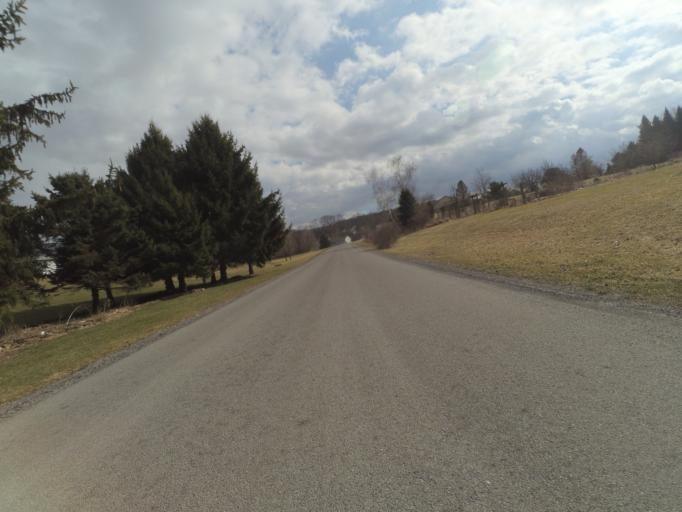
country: US
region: Pennsylvania
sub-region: Centre County
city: Stormstown
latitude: 40.7682
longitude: -78.0378
